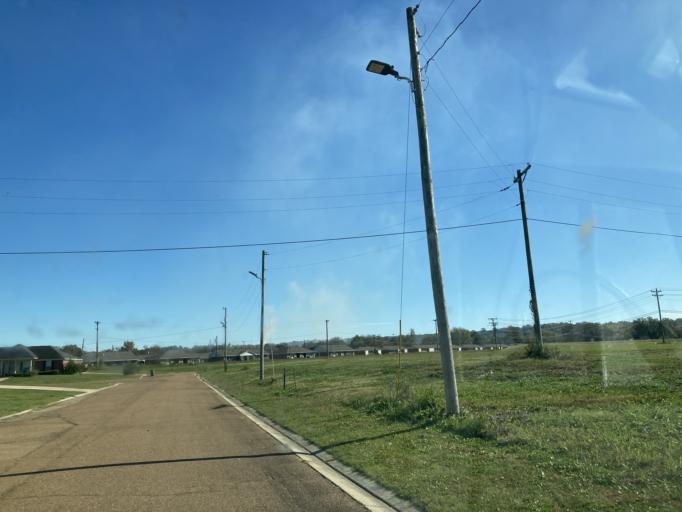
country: US
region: Mississippi
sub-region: Yazoo County
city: Yazoo City
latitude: 32.8568
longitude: -90.4287
